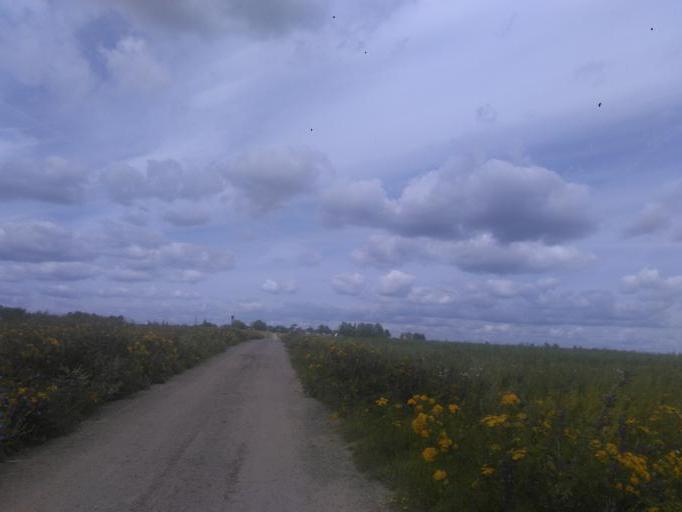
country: RU
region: Moskovskaya
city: Solnechnogorsk
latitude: 56.1406
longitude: 36.9284
